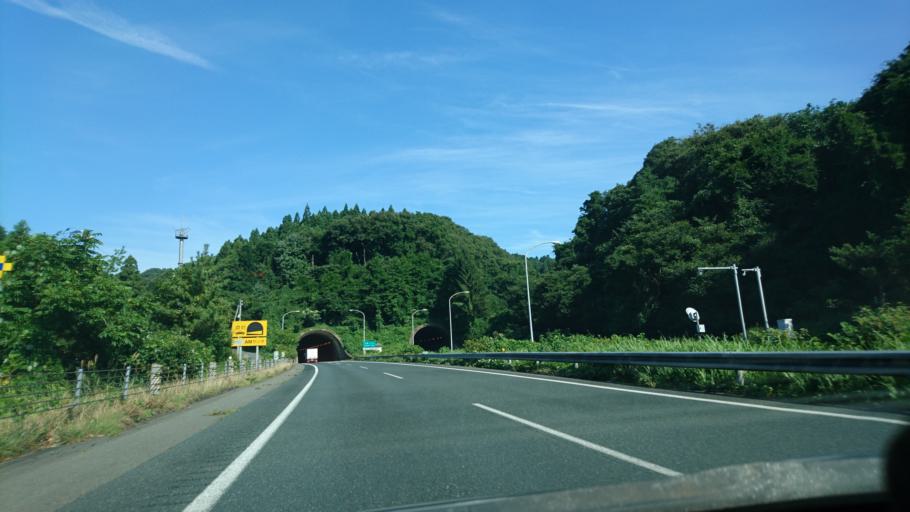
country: JP
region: Iwate
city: Ichinoseki
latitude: 38.9881
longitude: 141.1031
